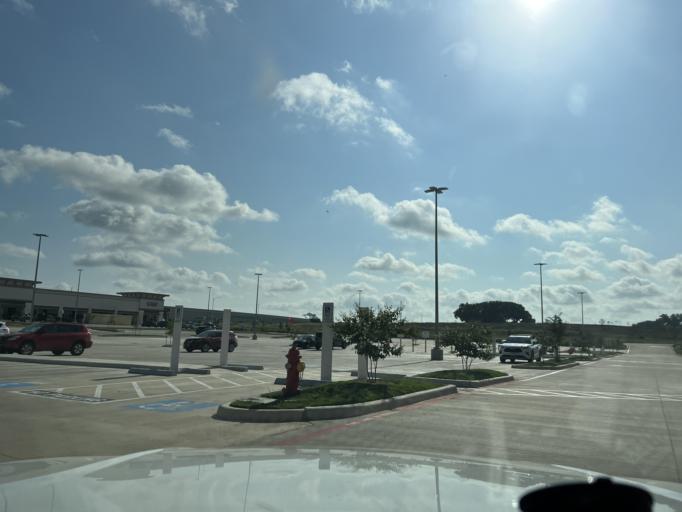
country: US
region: Texas
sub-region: Washington County
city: Brenham
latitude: 30.1405
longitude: -96.3827
